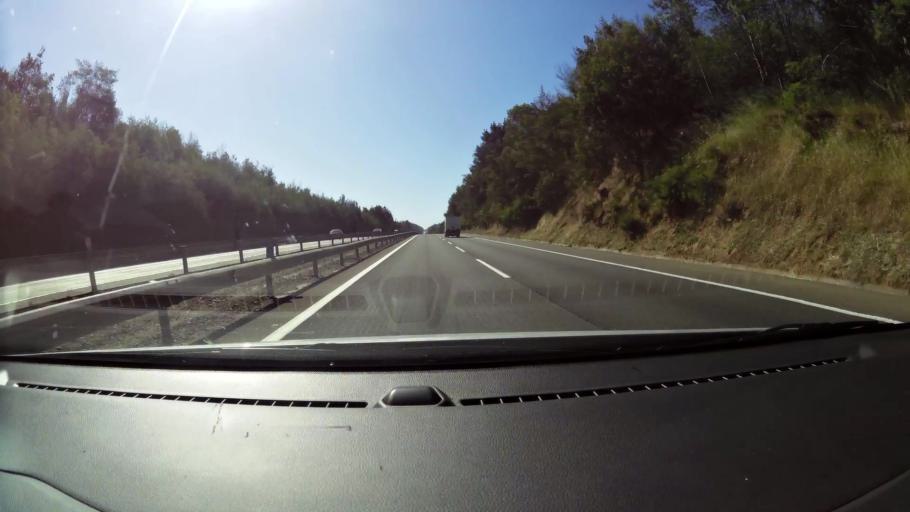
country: CL
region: Valparaiso
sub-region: Provincia de Marga Marga
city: Quilpue
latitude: -33.1772
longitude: -71.5105
